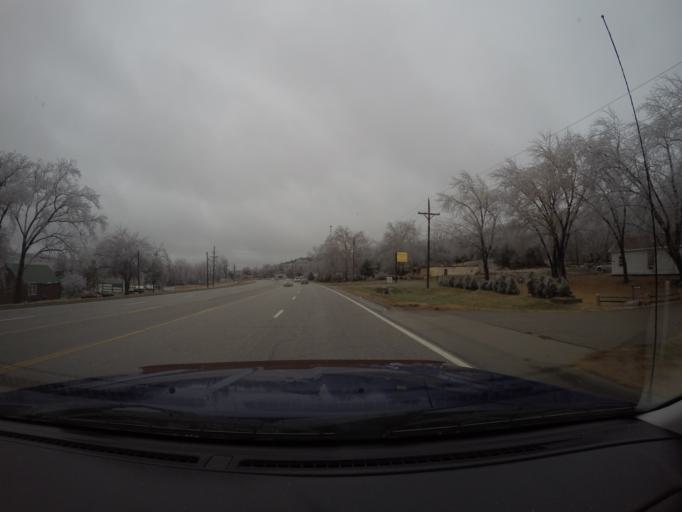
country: US
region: Kansas
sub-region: Riley County
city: Manhattan
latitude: 39.1679
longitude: -96.5409
